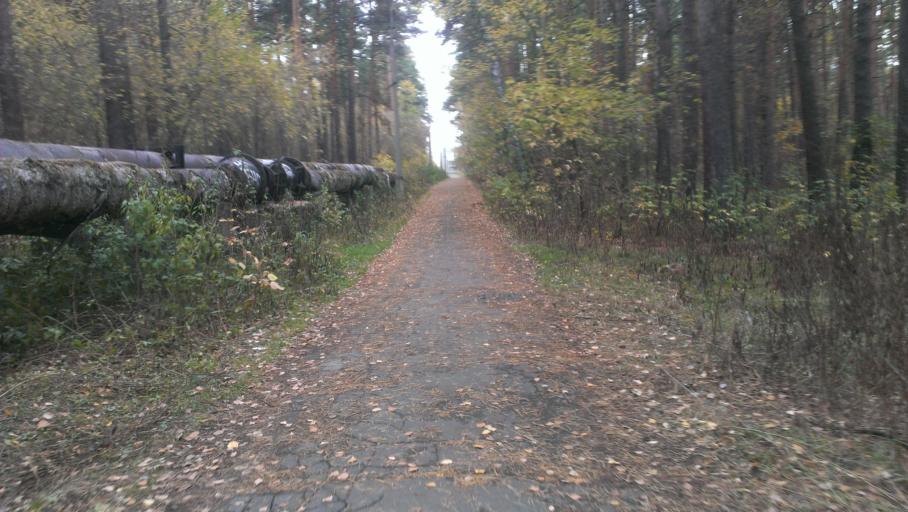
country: RU
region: Altai Krai
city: Yuzhnyy
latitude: 53.2602
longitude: 83.6886
